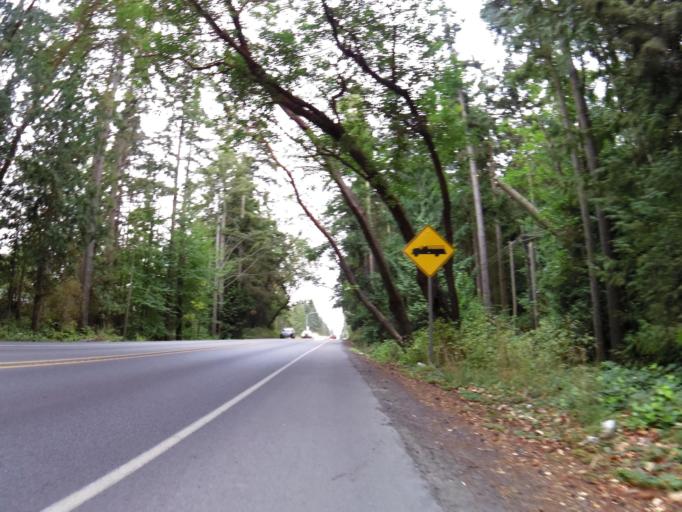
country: US
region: Washington
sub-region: Jefferson County
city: Port Hadlock-Irondale
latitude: 48.0852
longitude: -122.8170
